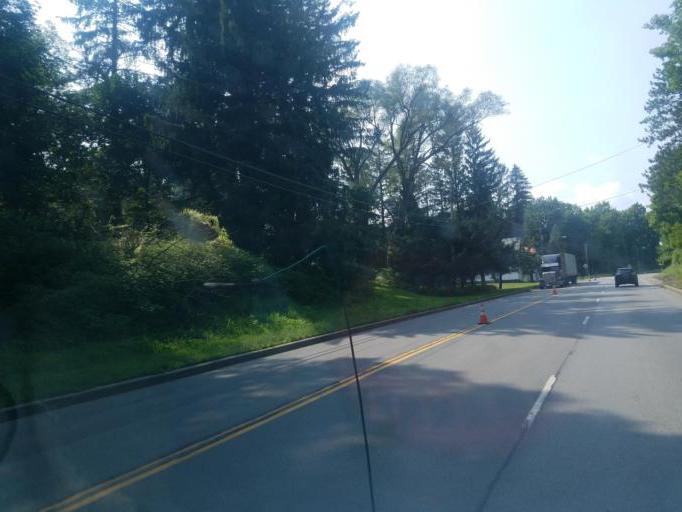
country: US
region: New York
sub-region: Montgomery County
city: Fonda
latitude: 42.9579
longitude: -74.3836
